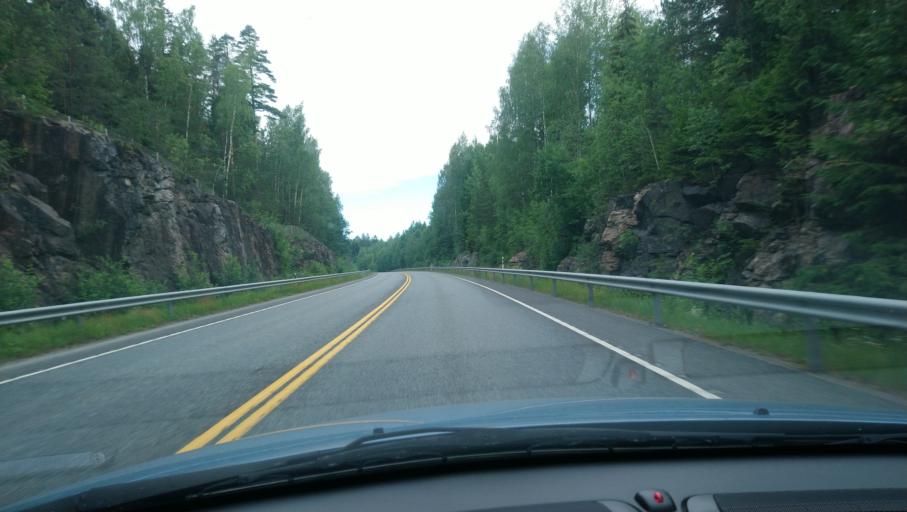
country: FI
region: Uusimaa
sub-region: Porvoo
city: Porvoo
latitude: 60.4255
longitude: 25.5797
